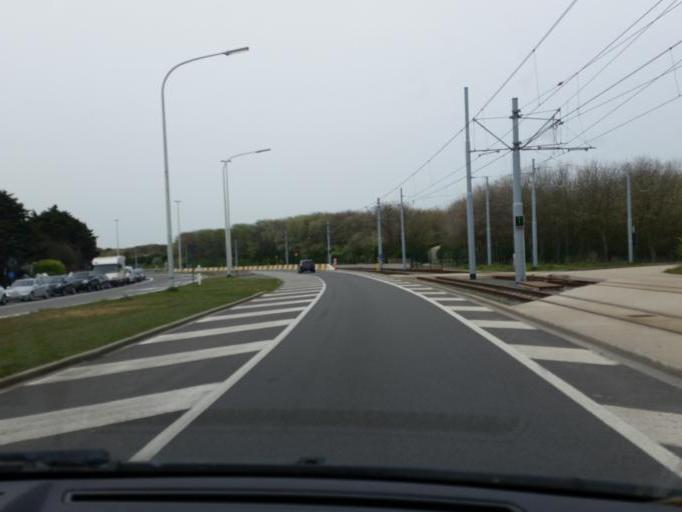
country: BE
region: Flanders
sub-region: Provincie West-Vlaanderen
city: Blankenberge
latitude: 51.3103
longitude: 3.1109
